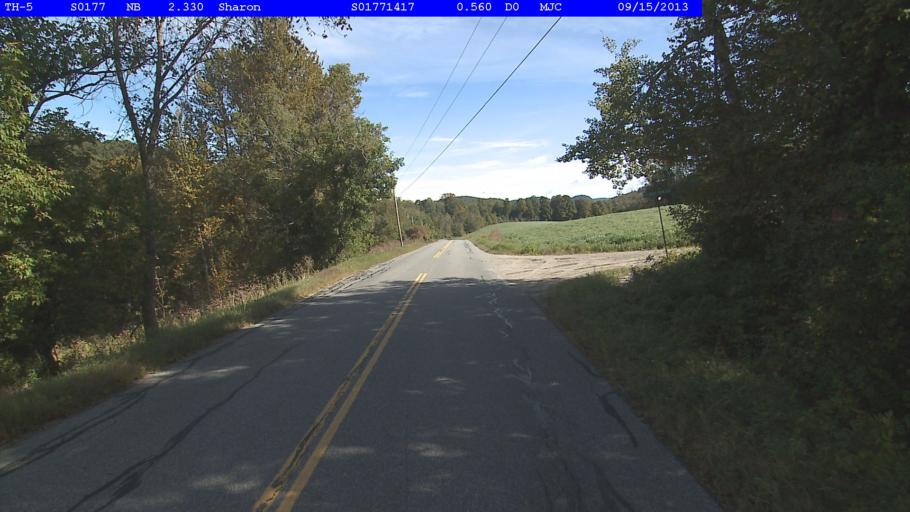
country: US
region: Vermont
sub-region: Windsor County
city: Woodstock
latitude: 43.7521
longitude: -72.4838
